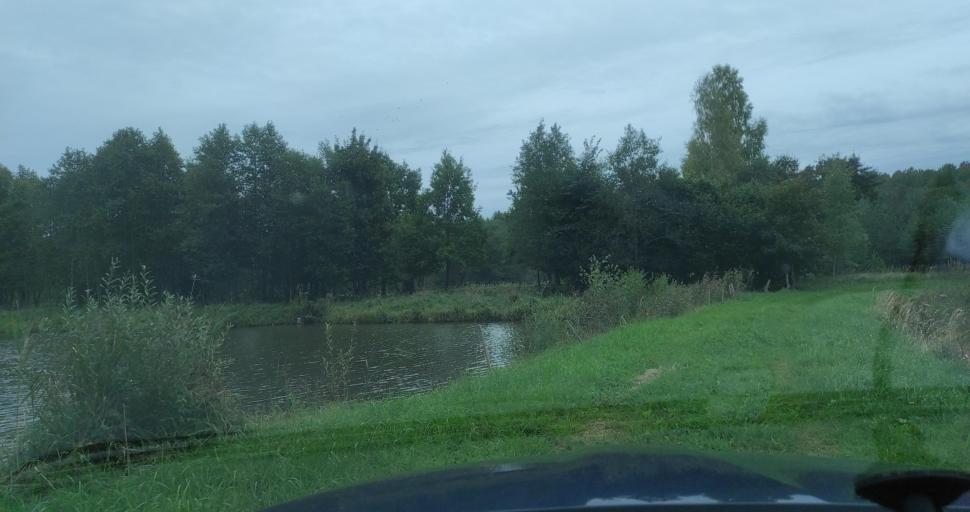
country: LV
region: Talsu Rajons
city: Stende
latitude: 57.0723
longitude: 22.3014
